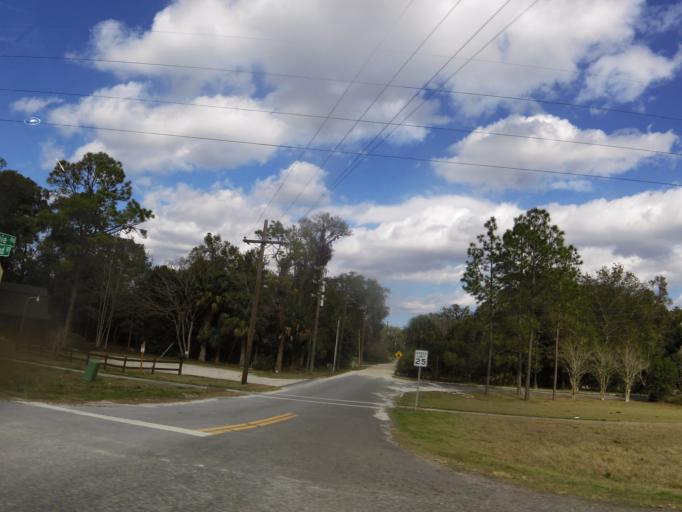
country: US
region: Florida
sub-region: Volusia County
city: De Leon Springs
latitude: 29.0869
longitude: -81.3233
